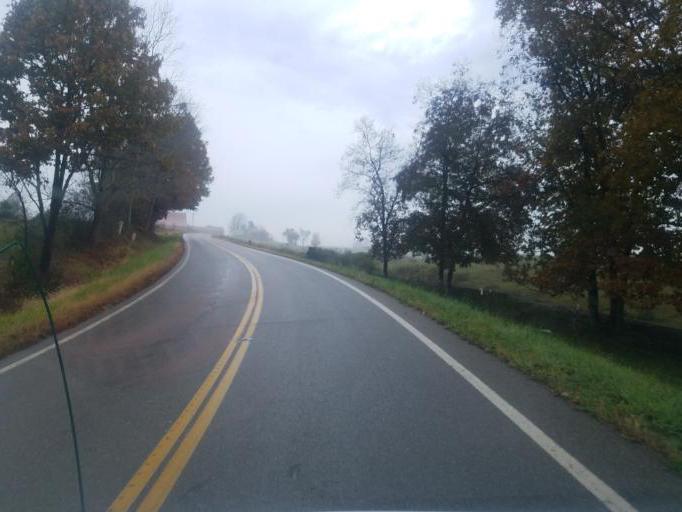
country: US
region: Ohio
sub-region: Morgan County
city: McConnelsville
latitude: 39.4741
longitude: -81.8780
